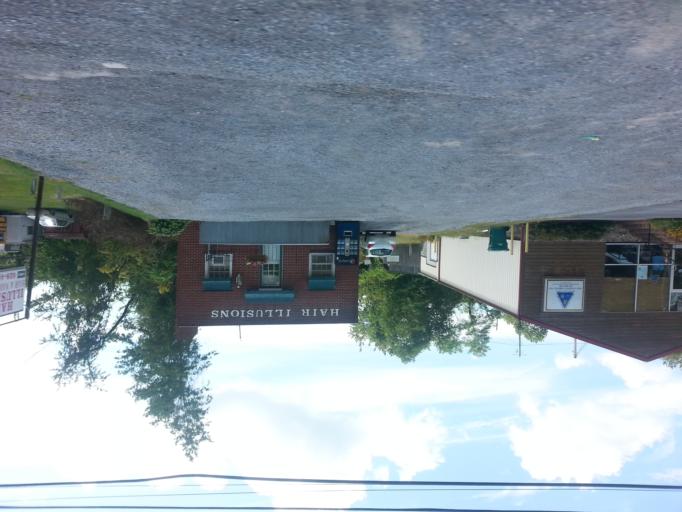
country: US
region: Virginia
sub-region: Washington County
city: Abingdon
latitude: 36.6950
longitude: -82.0181
